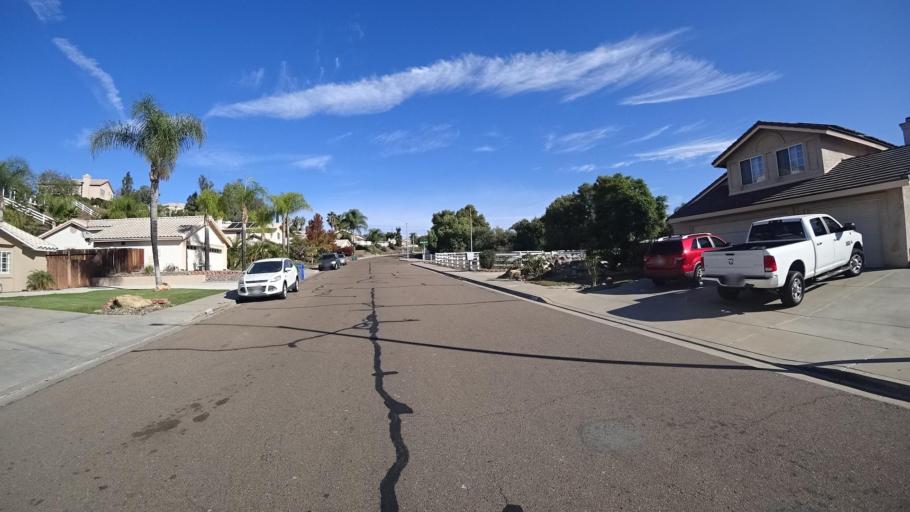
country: US
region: California
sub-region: San Diego County
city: Lakeside
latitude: 32.8438
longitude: -116.8911
